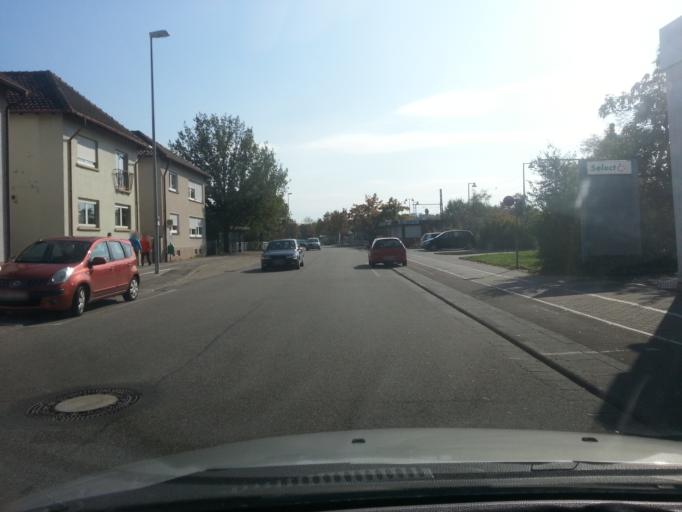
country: DE
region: Rheinland-Pfalz
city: Schifferstadt
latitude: 49.3753
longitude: 8.3766
